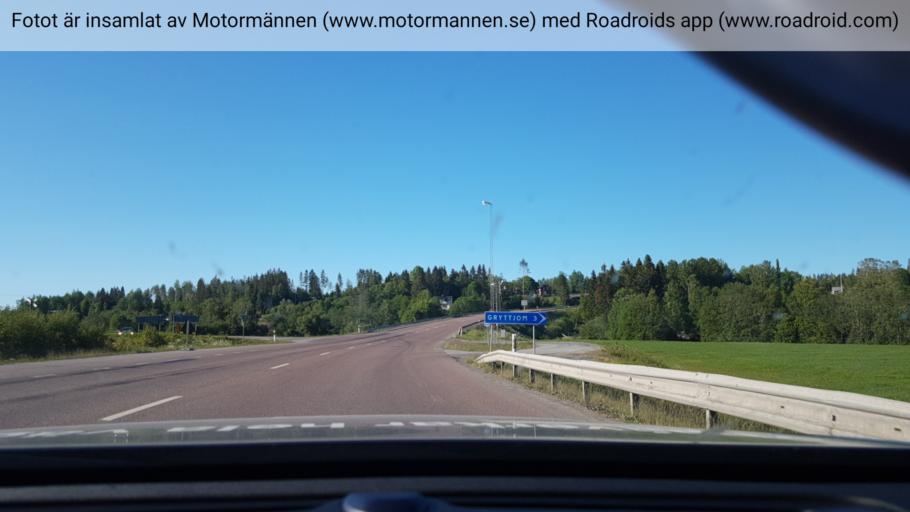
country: SE
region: Vaesternorrland
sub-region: Haernoesands Kommun
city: Haernoesand
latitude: 62.6850
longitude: 17.8467
